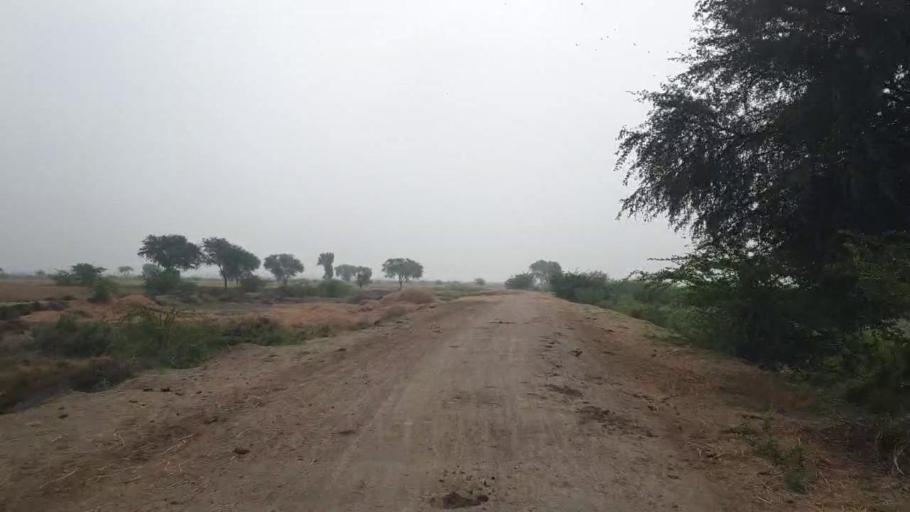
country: PK
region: Sindh
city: Badin
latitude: 24.5850
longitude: 68.6813
